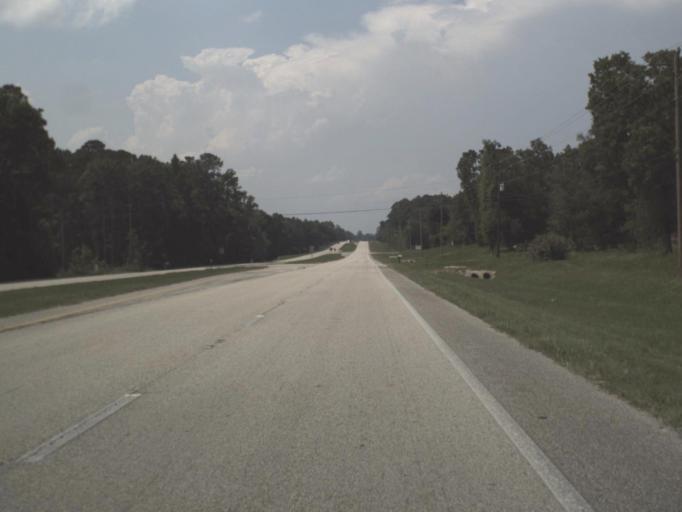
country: US
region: Florida
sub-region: Clay County
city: Green Cove Springs
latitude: 29.9167
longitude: -81.6808
